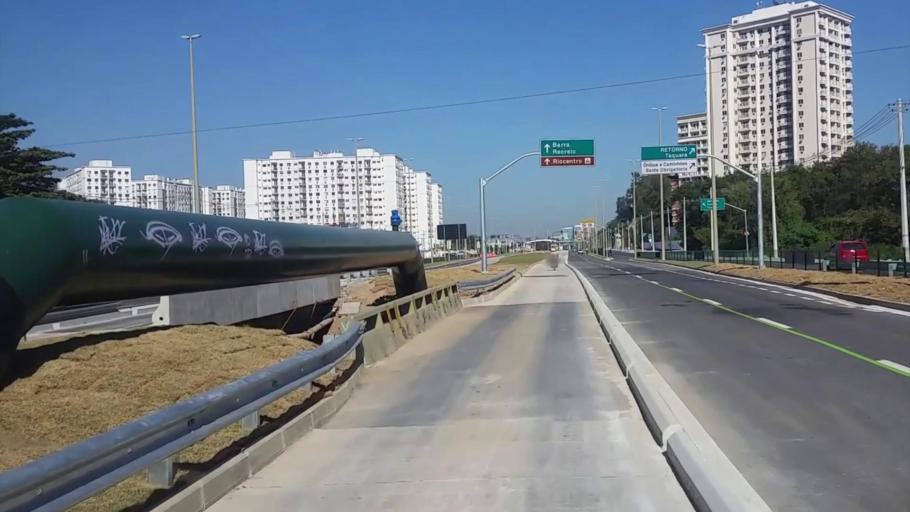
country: BR
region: Rio de Janeiro
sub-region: Nilopolis
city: Nilopolis
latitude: -22.9599
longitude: -43.3920
